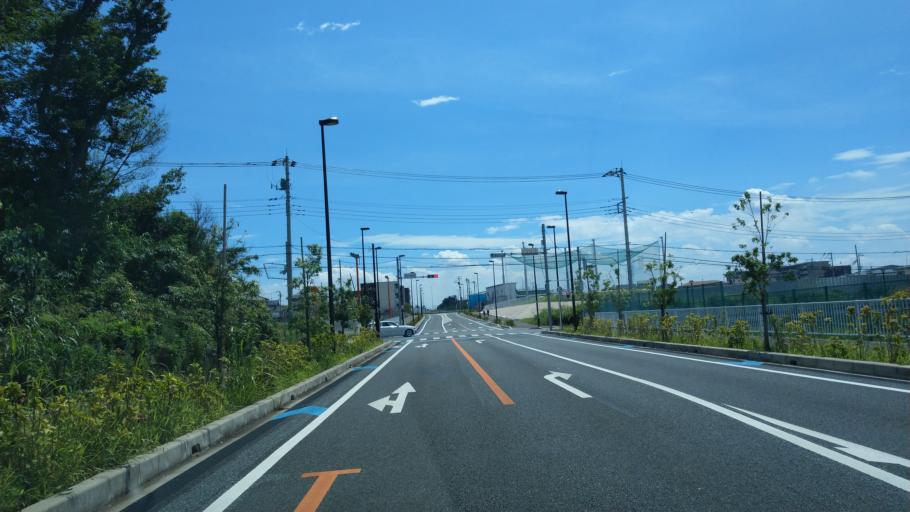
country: JP
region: Saitama
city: Ageoshimo
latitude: 35.9268
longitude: 139.5754
